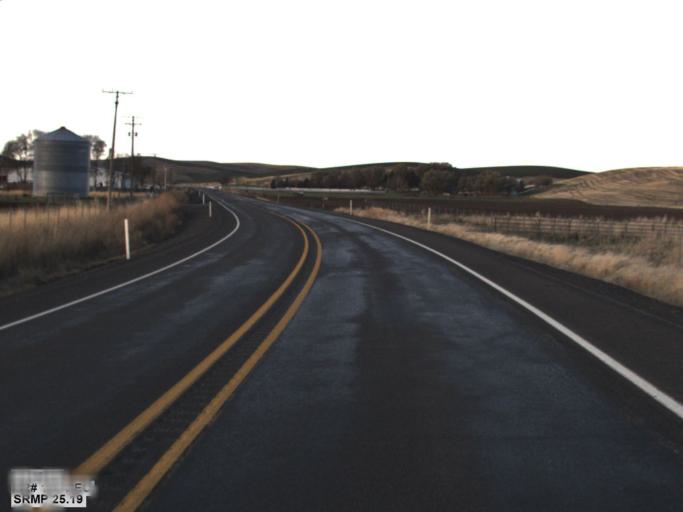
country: US
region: Washington
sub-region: Garfield County
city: Pomeroy
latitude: 46.7924
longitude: -117.6845
